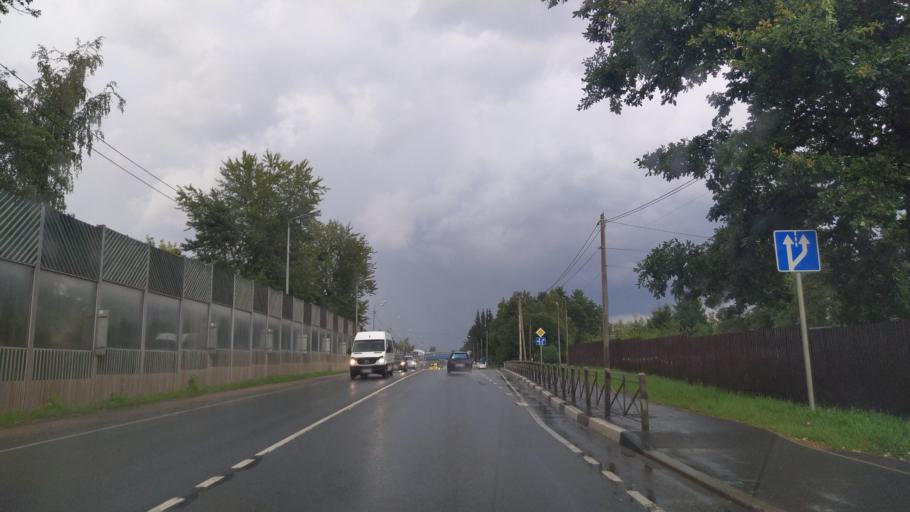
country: RU
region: Pskov
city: Pskov
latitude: 57.7574
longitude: 28.3828
